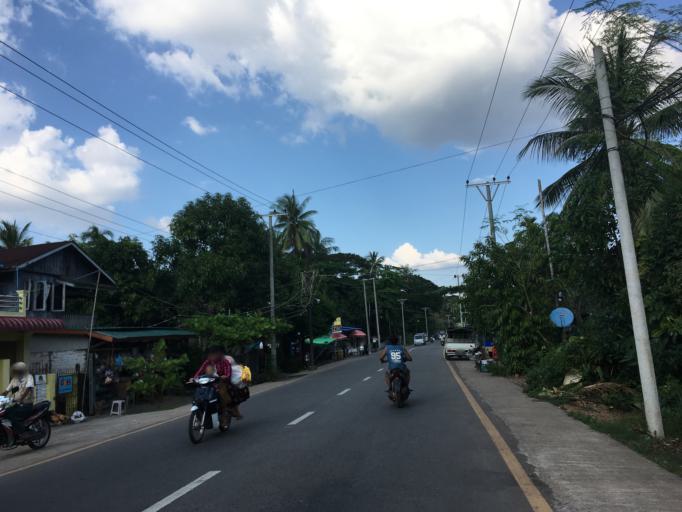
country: MM
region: Mon
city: Mawlamyine
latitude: 16.4454
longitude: 97.6200
